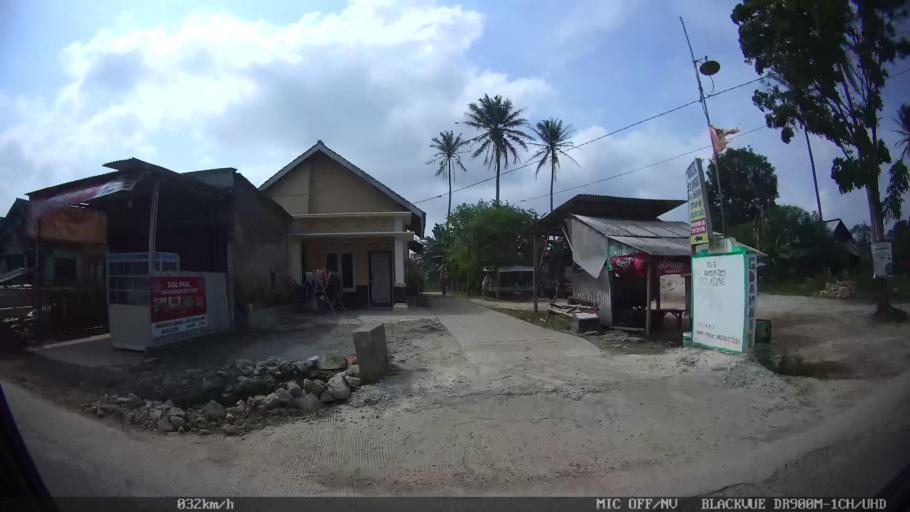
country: ID
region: Lampung
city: Kedaton
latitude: -5.3326
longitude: 105.2806
